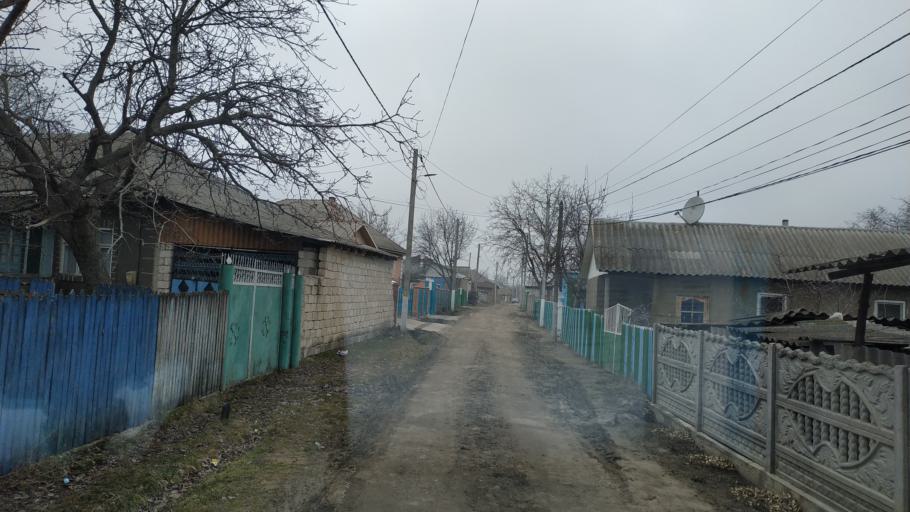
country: MD
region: Hincesti
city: Hincesti
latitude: 46.8928
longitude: 28.5462
